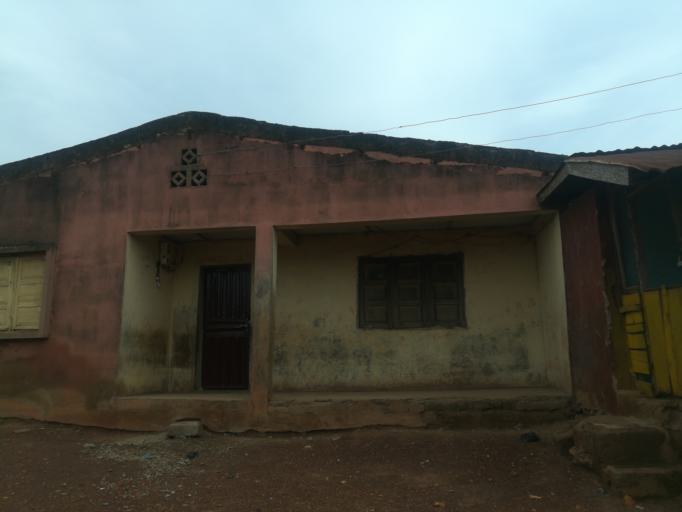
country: NG
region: Oyo
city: Ibadan
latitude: 7.3750
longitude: 3.9534
